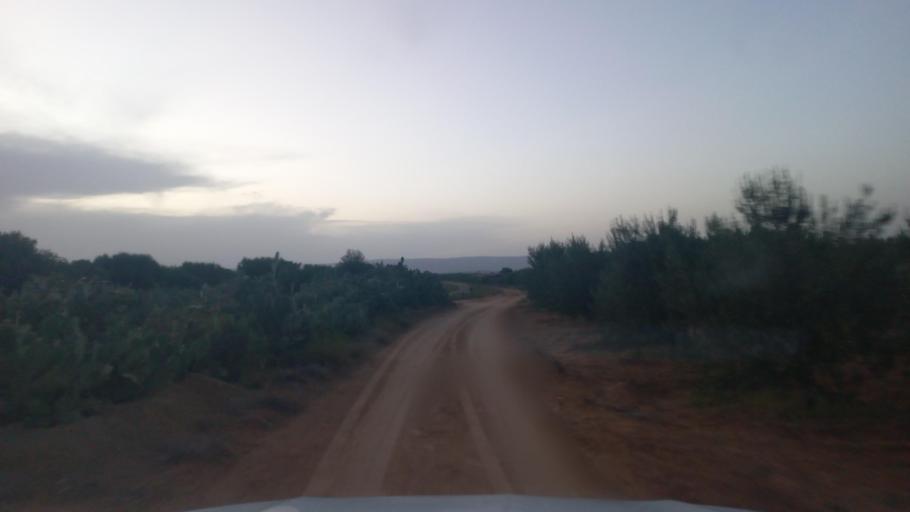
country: TN
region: Al Qasrayn
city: Kasserine
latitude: 35.2296
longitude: 9.0362
